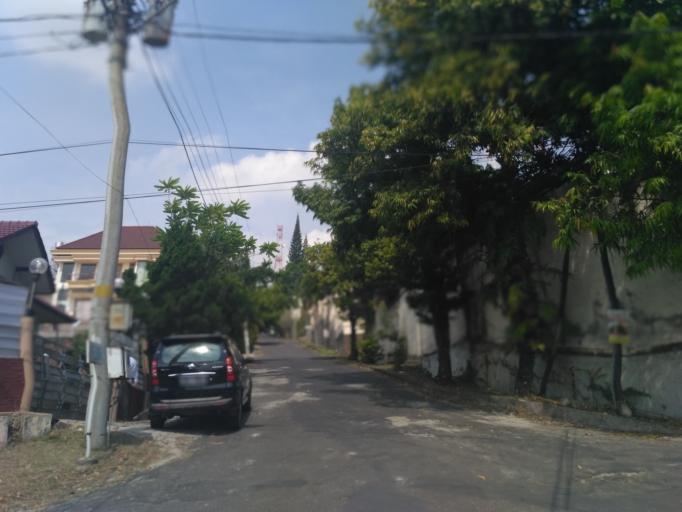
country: ID
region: Central Java
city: Semarang
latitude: -7.0433
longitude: 110.4278
